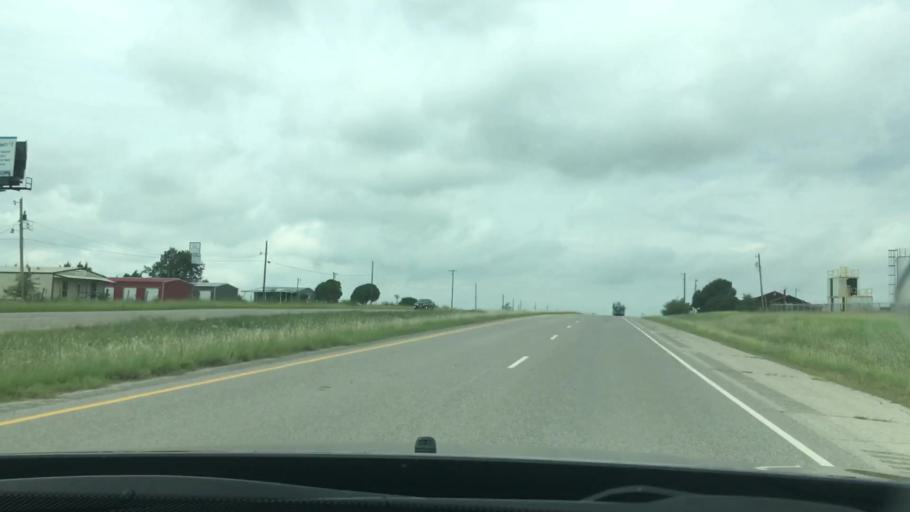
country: US
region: Oklahoma
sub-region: Carter County
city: Wilson
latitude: 34.1732
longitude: -97.4401
